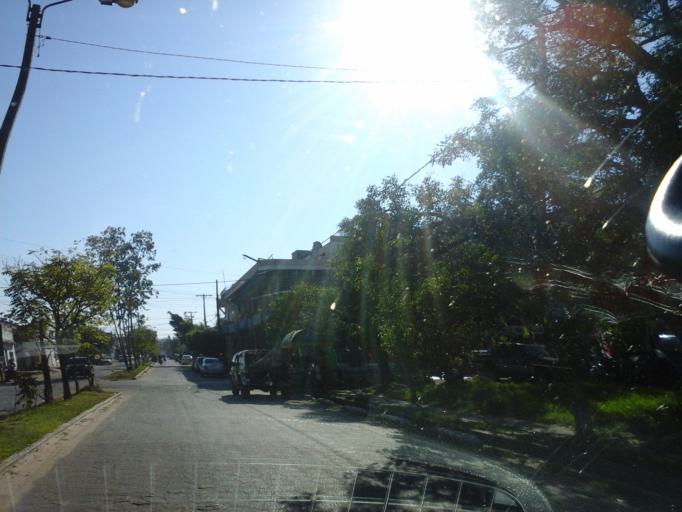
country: PY
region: Neembucu
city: Pilar
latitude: -26.8608
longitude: -58.3007
